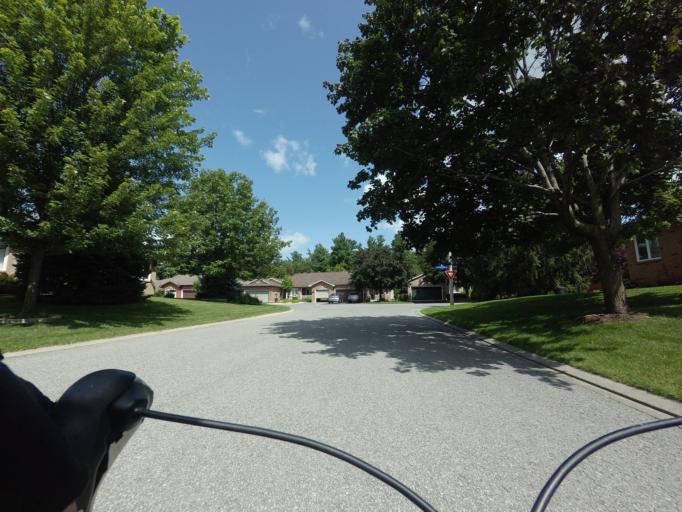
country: CA
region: Ontario
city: Bells Corners
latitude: 45.2920
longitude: -75.8462
